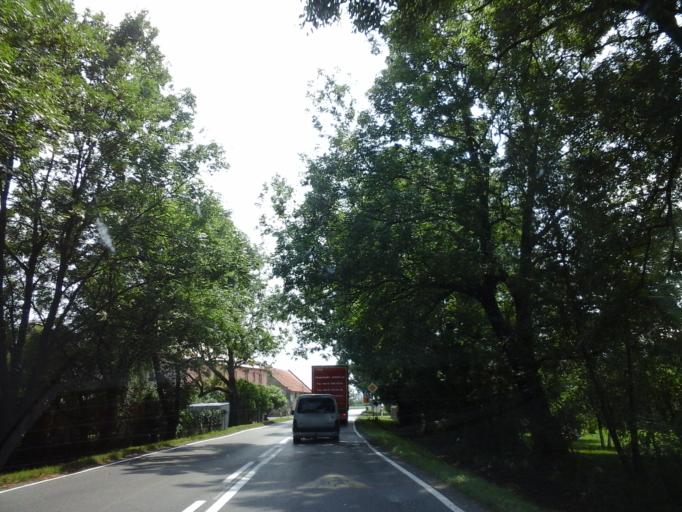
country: PL
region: Lower Silesian Voivodeship
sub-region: Powiat wroclawski
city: Zorawina
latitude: 50.9422
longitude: 17.0705
